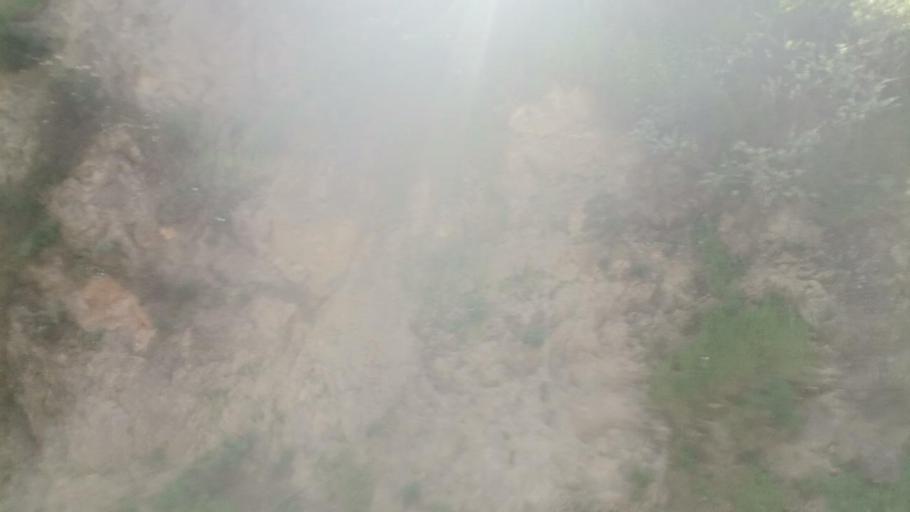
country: CL
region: Valparaiso
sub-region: Provincia de Marga Marga
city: Limache
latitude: -33.1961
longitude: -71.2722
